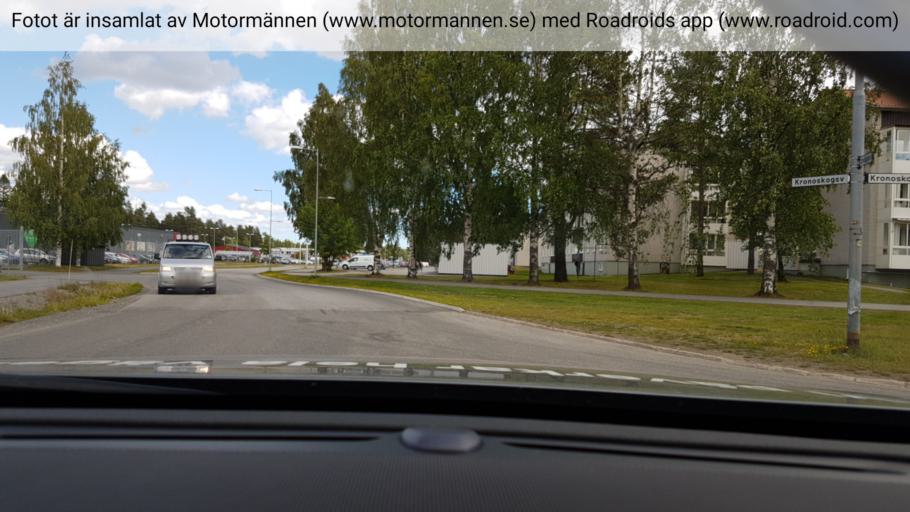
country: SE
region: Vaesterbotten
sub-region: Umea Kommun
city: Roback
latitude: 63.8405
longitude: 20.1887
